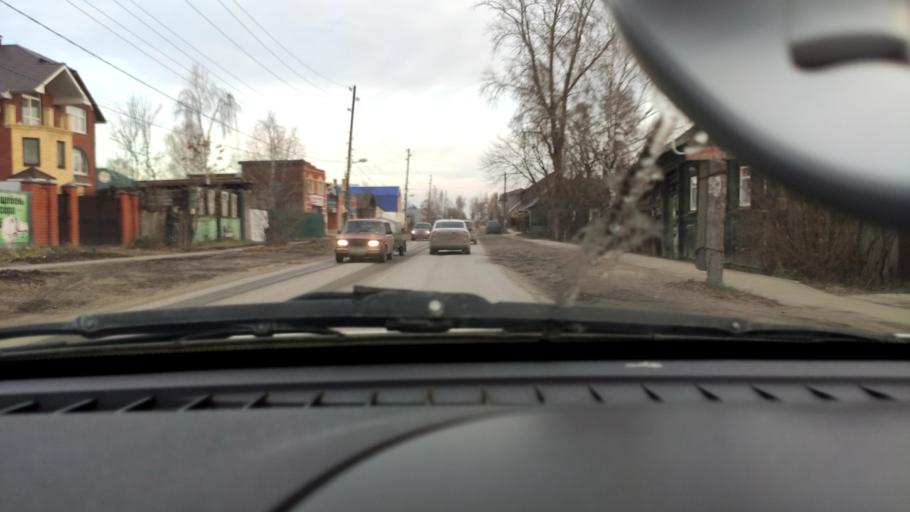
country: RU
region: Perm
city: Perm
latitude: 58.0435
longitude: 56.3277
